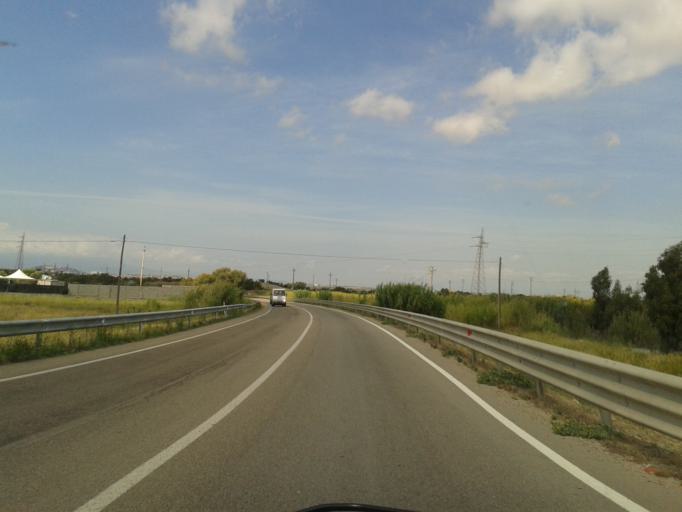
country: IT
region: Sardinia
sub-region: Provincia di Cagliari
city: Maracalagonis
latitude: 39.2694
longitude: 9.2055
